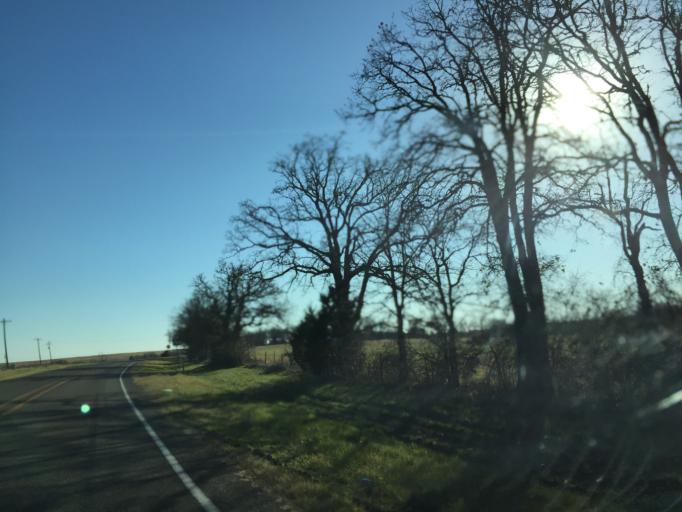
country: US
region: Texas
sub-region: Bastrop County
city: Elgin
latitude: 30.3845
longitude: -97.2437
